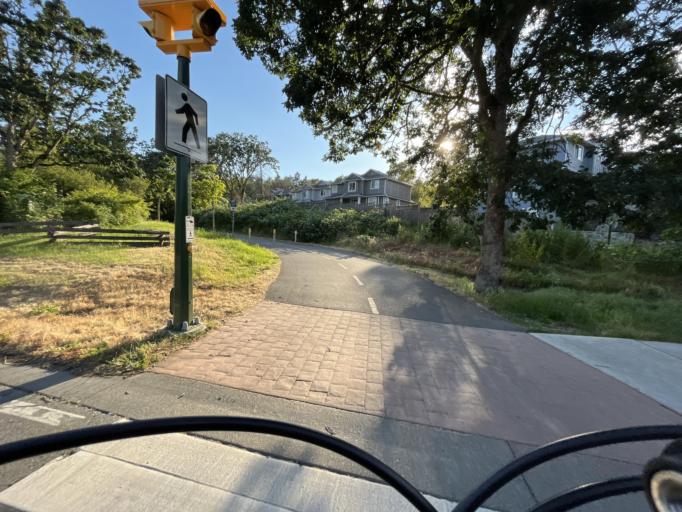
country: CA
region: British Columbia
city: Colwood
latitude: 48.4576
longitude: -123.4661
